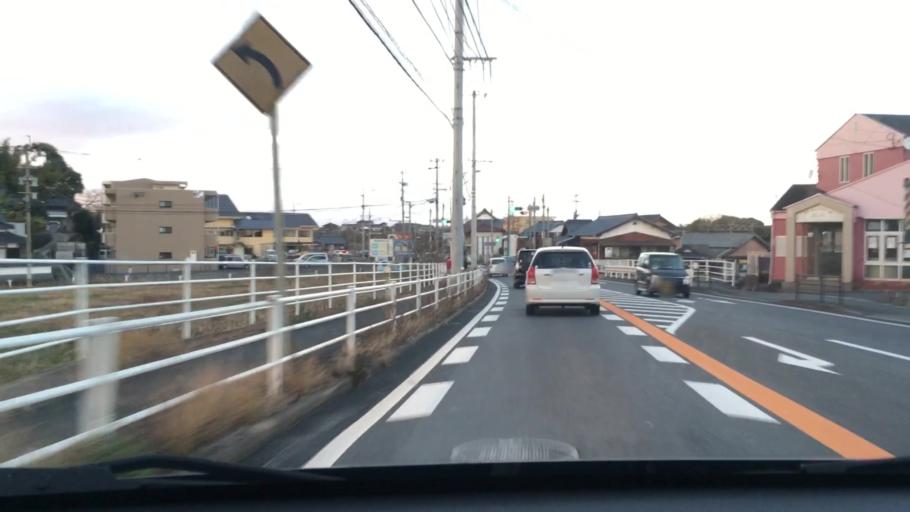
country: JP
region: Fukuoka
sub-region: Buzen-shi
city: Buzen
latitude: 33.6214
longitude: 131.0950
